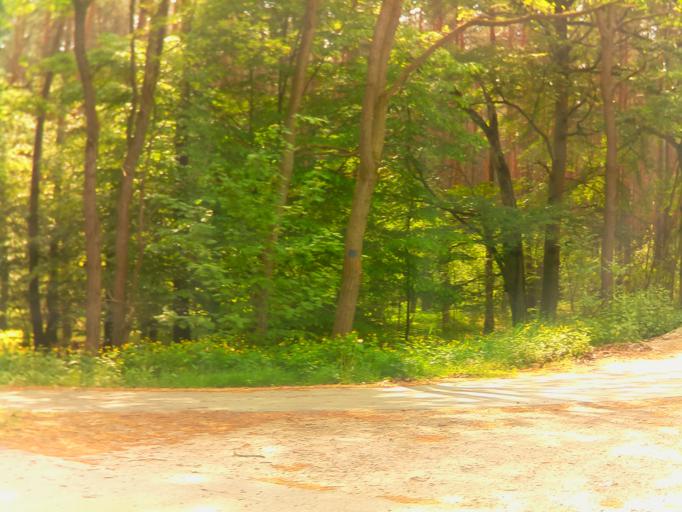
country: DE
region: Brandenburg
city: Rathenow
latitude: 52.6045
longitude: 12.3930
